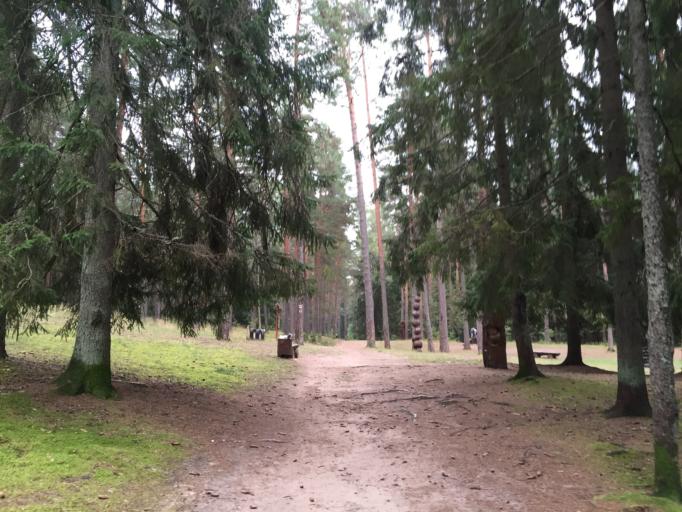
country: LV
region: Ogre
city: Ogre
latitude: 56.8294
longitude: 24.5865
